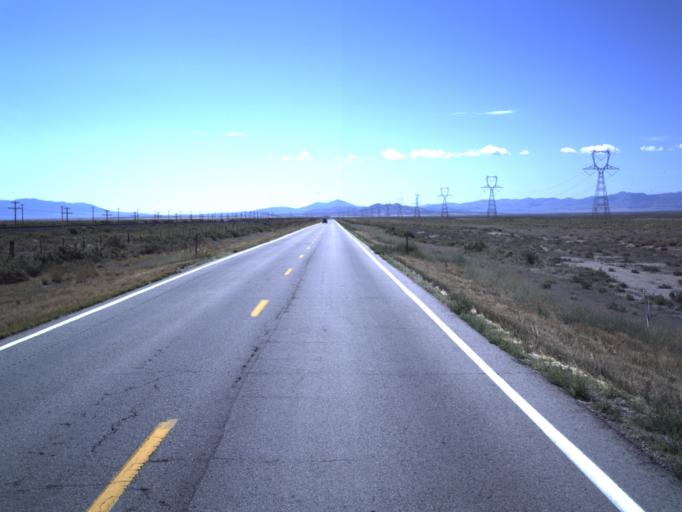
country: US
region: Utah
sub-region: Tooele County
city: Tooele
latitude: 40.3118
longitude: -112.4047
